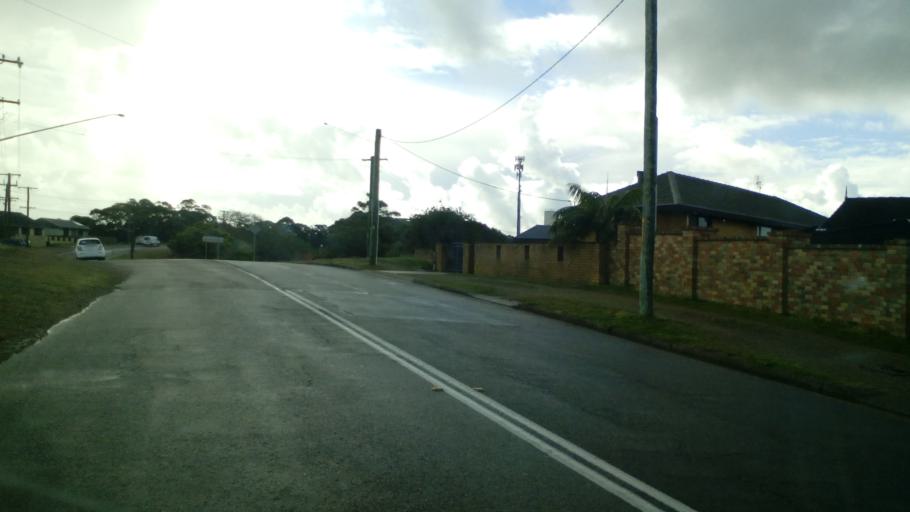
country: AU
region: New South Wales
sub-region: Lake Macquarie Shire
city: Kahibah
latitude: -32.9883
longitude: 151.7152
